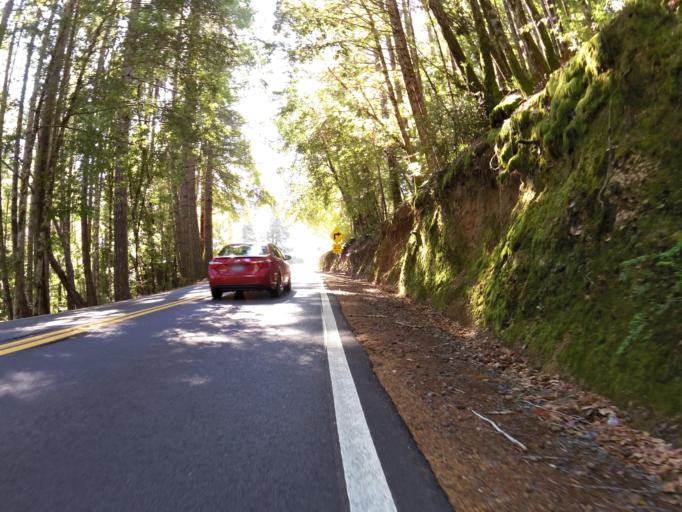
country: US
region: California
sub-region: Humboldt County
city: Redway
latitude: 39.8500
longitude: -123.7350
